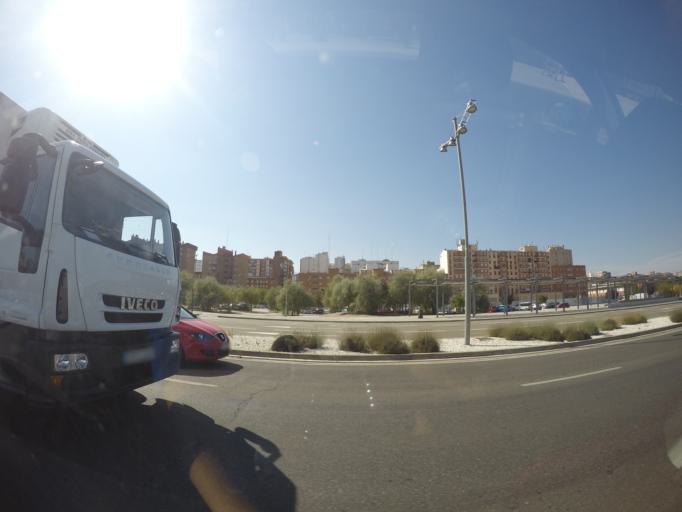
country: ES
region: Aragon
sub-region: Provincia de Zaragoza
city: Almozara
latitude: 41.6574
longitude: -0.9042
